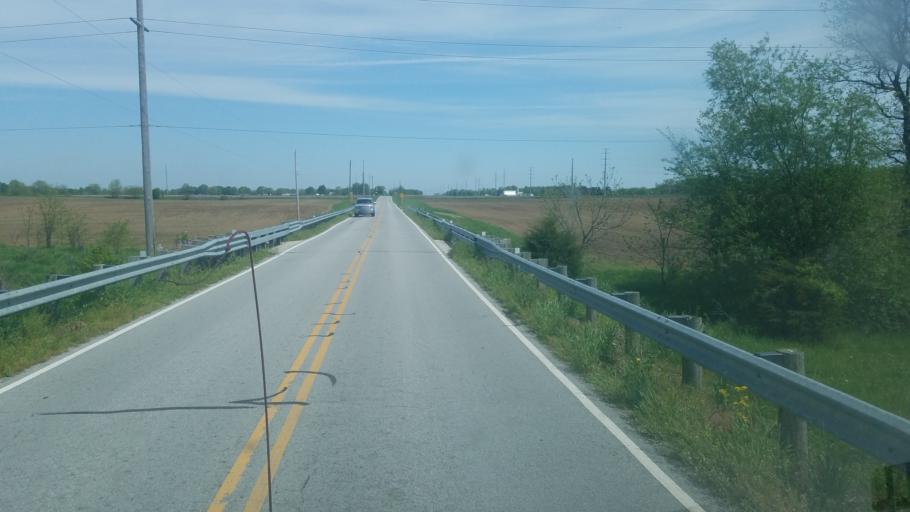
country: US
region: Ohio
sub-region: Seneca County
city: Tiffin
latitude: 41.1120
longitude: -83.1311
